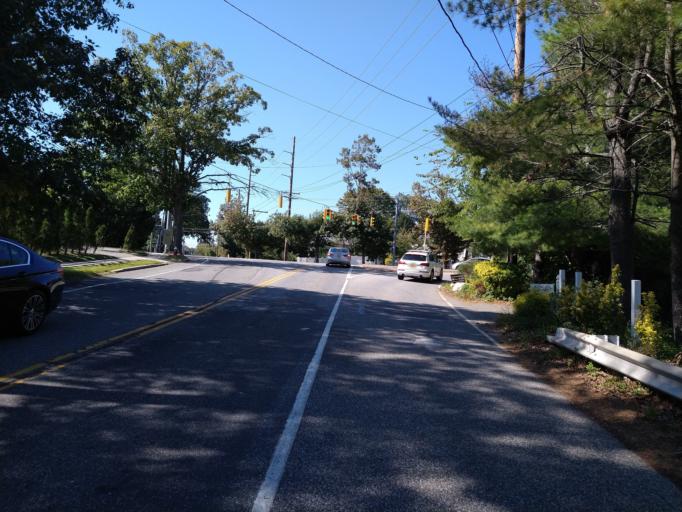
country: US
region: New York
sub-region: Nassau County
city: Syosset
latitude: 40.8278
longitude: -73.4932
